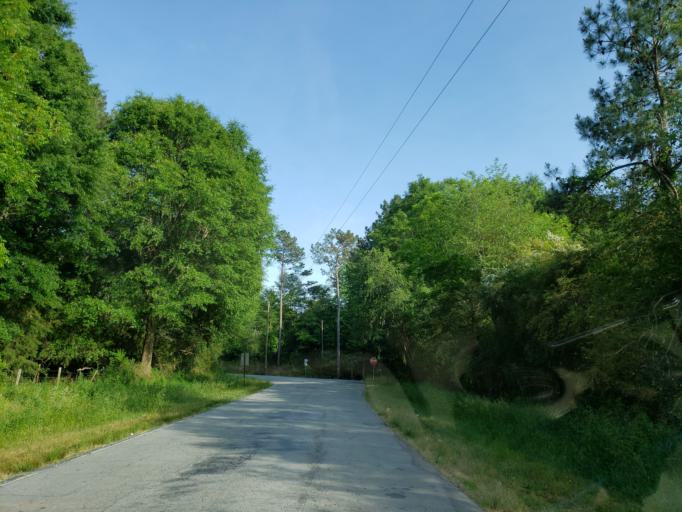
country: US
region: Georgia
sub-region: Carroll County
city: Bowdon
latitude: 33.4699
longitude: -85.2968
